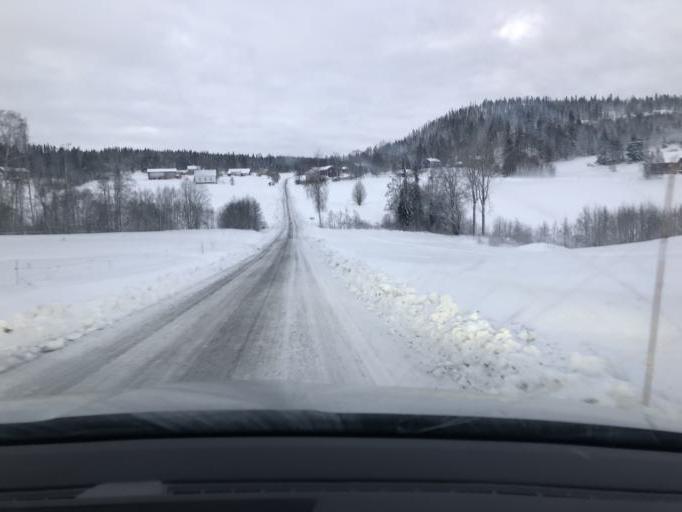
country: SE
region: Vaesternorrland
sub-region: Kramfors Kommun
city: Nordingra
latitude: 62.9111
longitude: 18.2359
